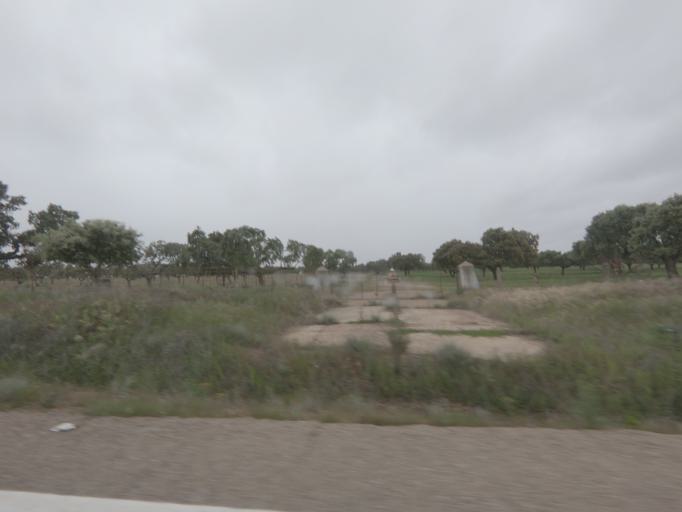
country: ES
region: Extremadura
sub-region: Provincia de Badajoz
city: Badajoz
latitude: 38.9581
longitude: -6.9050
